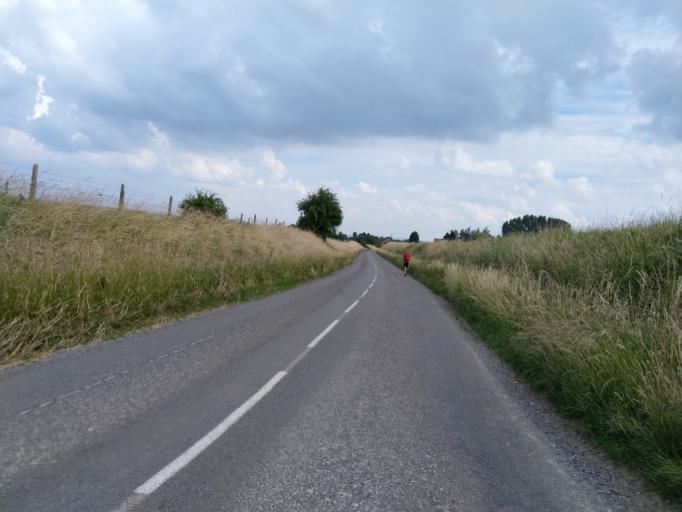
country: FR
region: Nord-Pas-de-Calais
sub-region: Departement du Nord
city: Boussois
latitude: 50.3313
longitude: 4.0102
